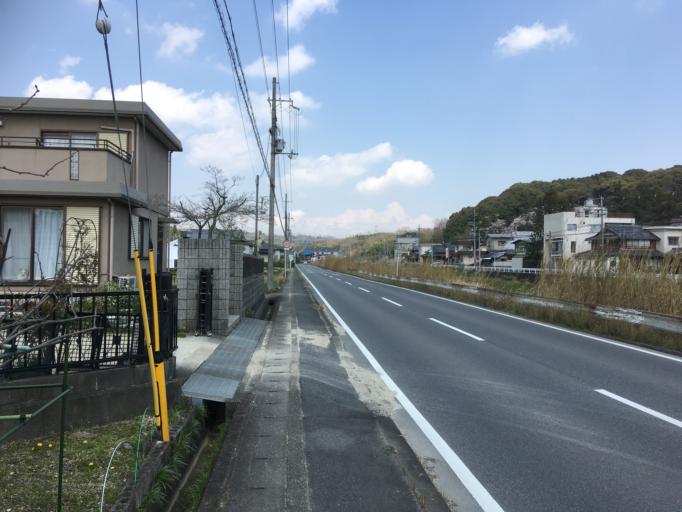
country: JP
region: Nara
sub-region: Ikoma-shi
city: Ikoma
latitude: 34.7429
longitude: 135.7212
